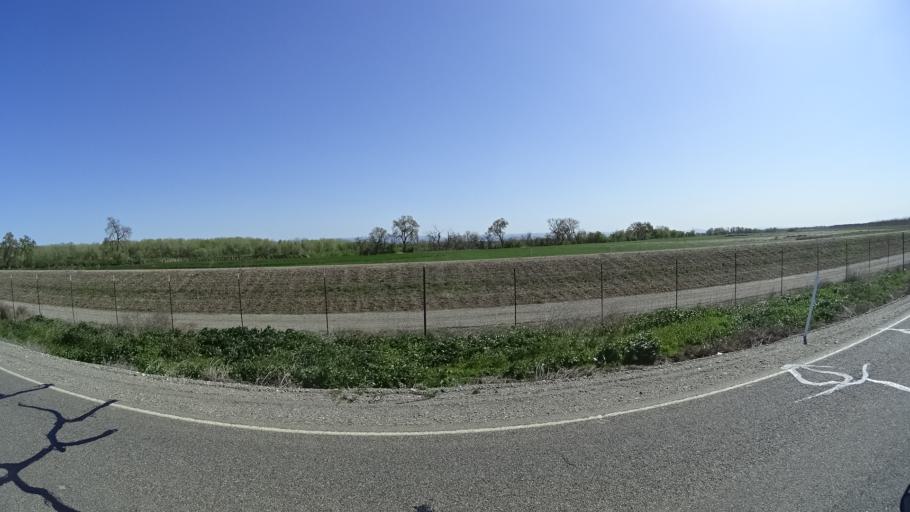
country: US
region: California
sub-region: Glenn County
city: Hamilton City
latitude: 39.7619
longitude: -122.0282
